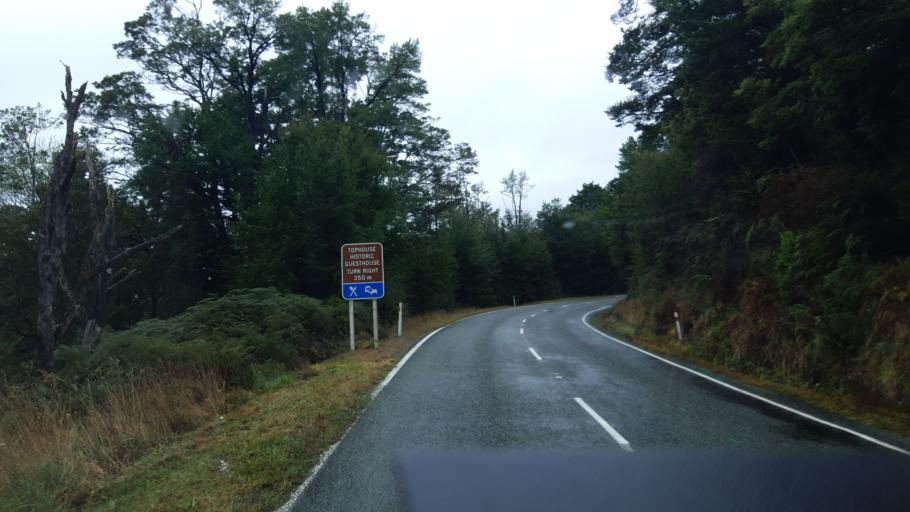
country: NZ
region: Tasman
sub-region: Tasman District
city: Wakefield
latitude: -41.7614
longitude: 172.8970
